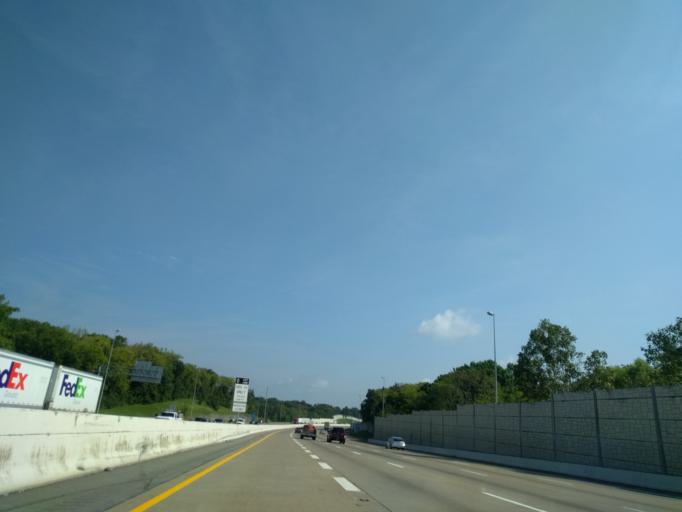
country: US
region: Tennessee
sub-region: Davidson County
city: Goodlettsville
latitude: 36.2744
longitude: -86.7356
